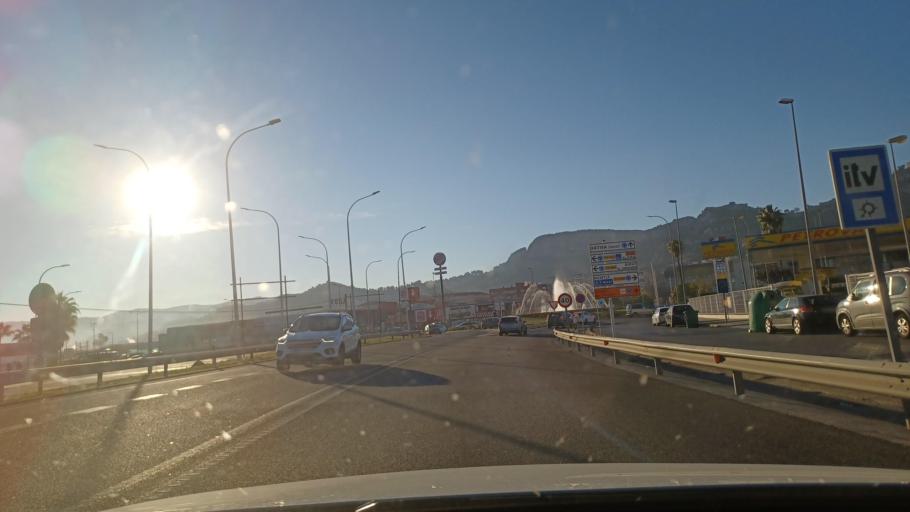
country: ES
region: Valencia
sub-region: Provincia de Valencia
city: Xativa
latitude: 38.9970
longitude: -0.5217
